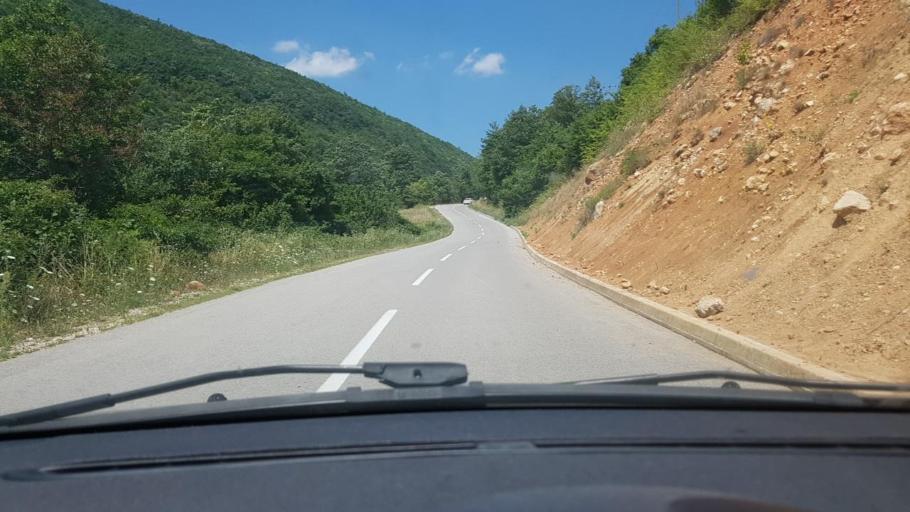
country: BA
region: Federation of Bosnia and Herzegovina
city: Orasac
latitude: 44.4991
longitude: 16.1324
